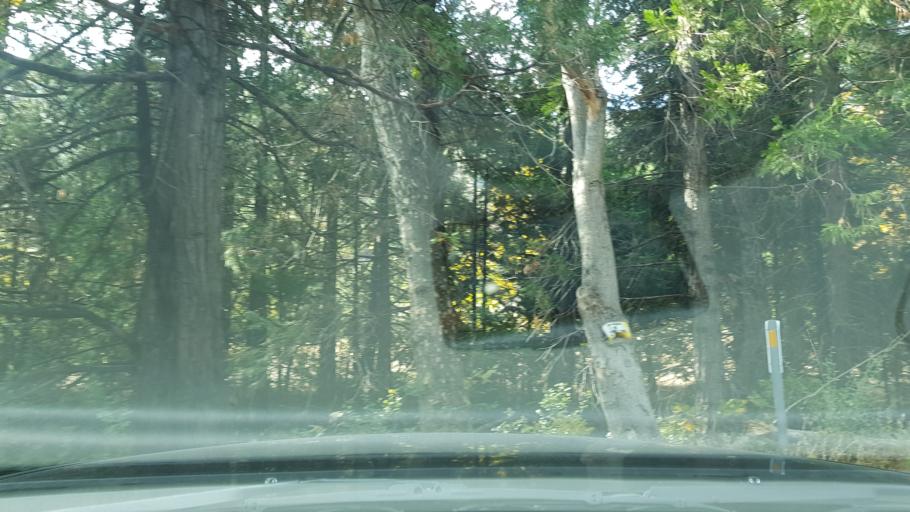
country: US
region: California
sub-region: San Diego County
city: Julian
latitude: 33.1267
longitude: -116.6015
